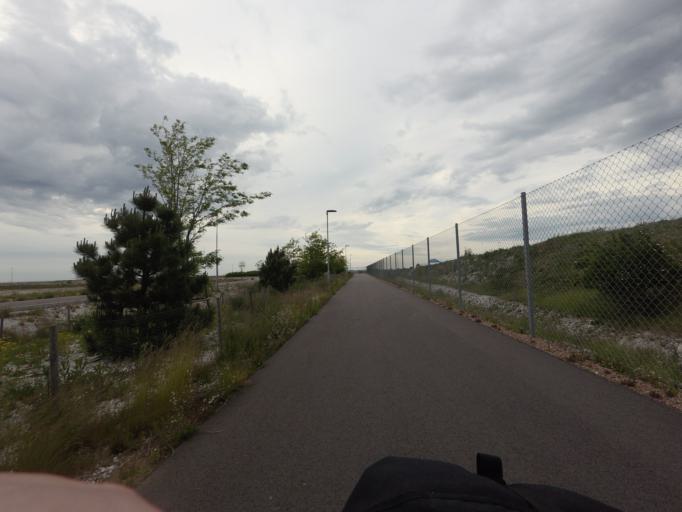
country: SE
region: Skane
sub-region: Malmo
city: Malmoe
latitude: 55.6338
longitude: 13.0065
